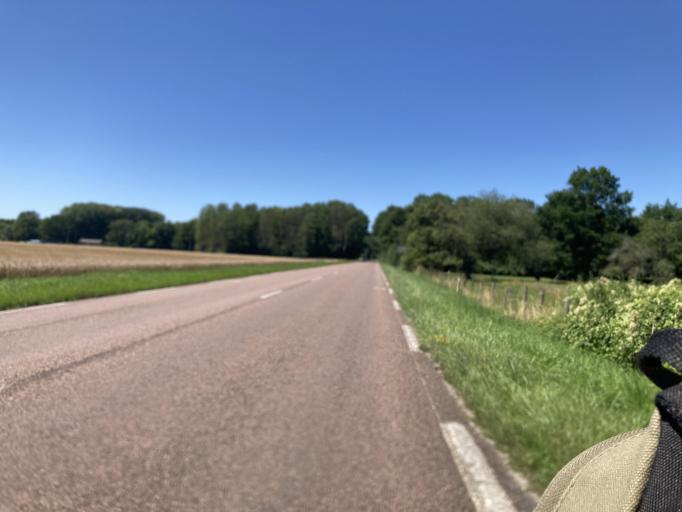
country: FR
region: Bourgogne
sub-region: Departement de l'Yonne
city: Laroche-Saint-Cydroine
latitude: 47.9652
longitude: 3.4681
